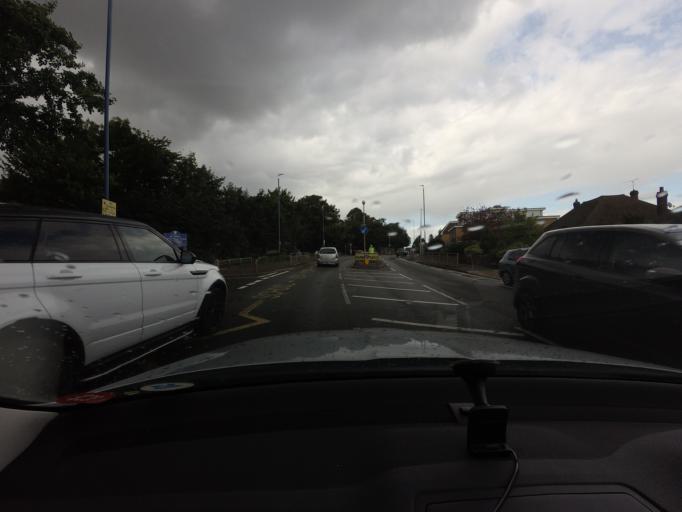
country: GB
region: England
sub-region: Kent
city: Gravesend
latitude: 51.4372
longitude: 0.3879
